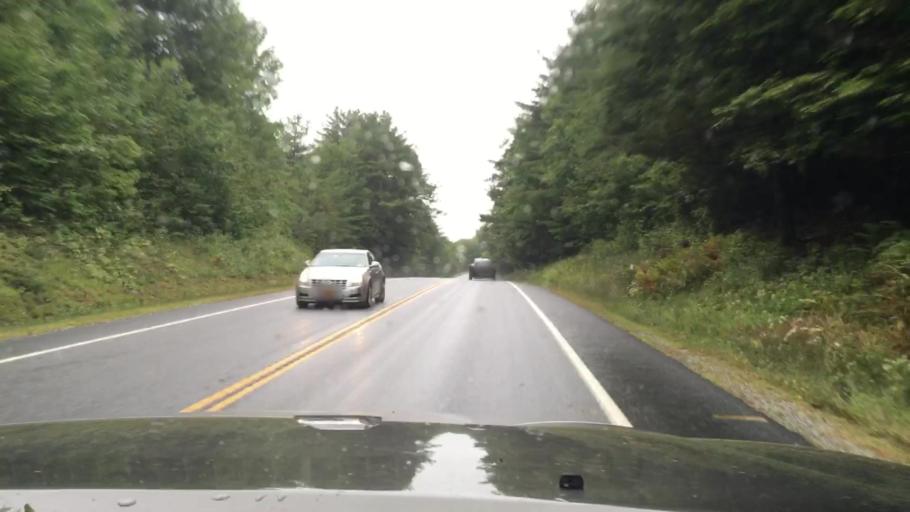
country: US
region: New Hampshire
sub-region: Hillsborough County
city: Antrim
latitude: 43.0697
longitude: -72.0528
